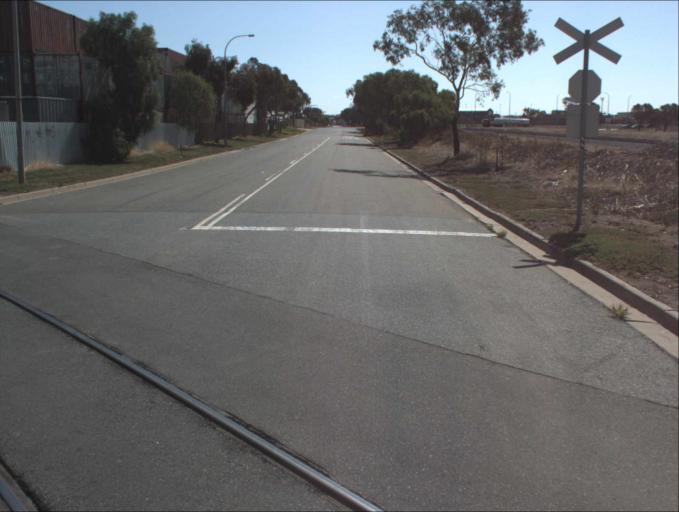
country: AU
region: South Australia
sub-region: Charles Sturt
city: Woodville North
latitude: -34.8402
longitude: 138.5492
